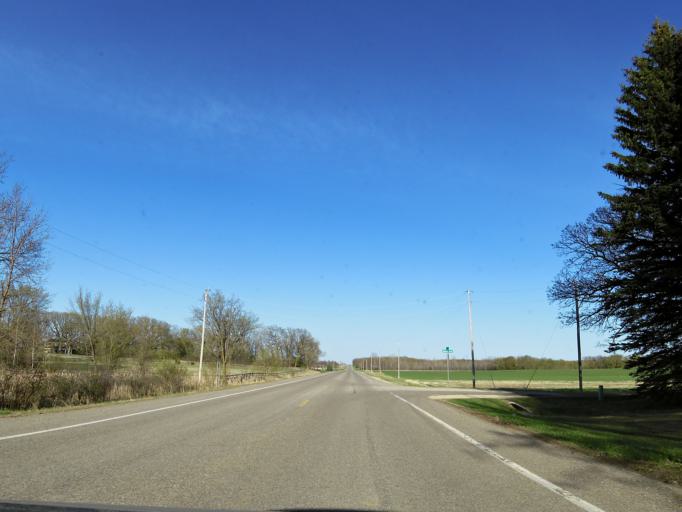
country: US
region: Minnesota
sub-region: Dakota County
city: Lakeville
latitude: 44.5873
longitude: -93.2590
